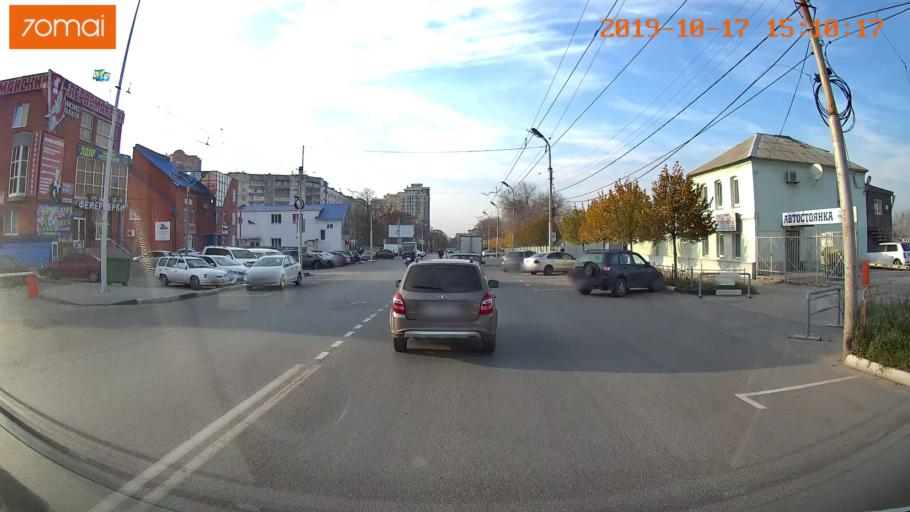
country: RU
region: Rjazan
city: Ryazan'
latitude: 54.6303
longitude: 39.7203
